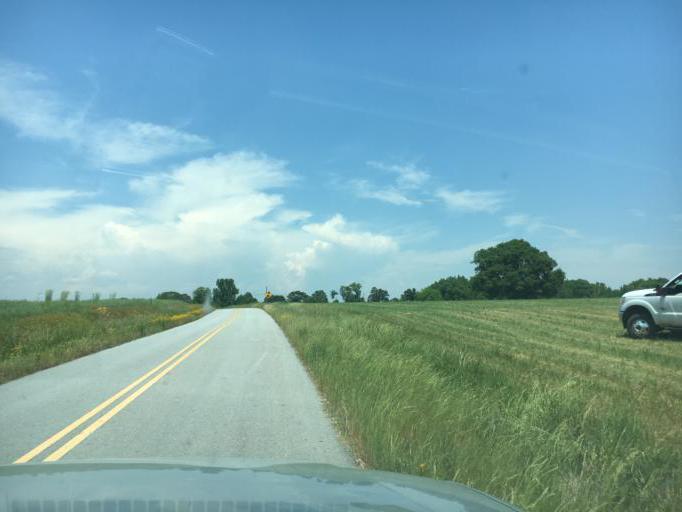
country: US
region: Georgia
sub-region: Hart County
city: Royston
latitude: 34.3238
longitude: -83.1017
